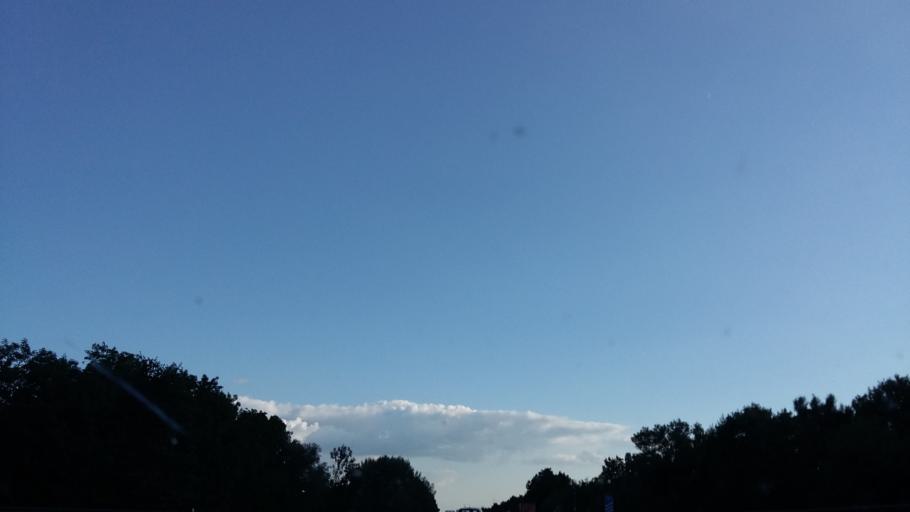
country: DE
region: Bavaria
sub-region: Swabia
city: Kellmunz
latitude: 48.1345
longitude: 10.1103
